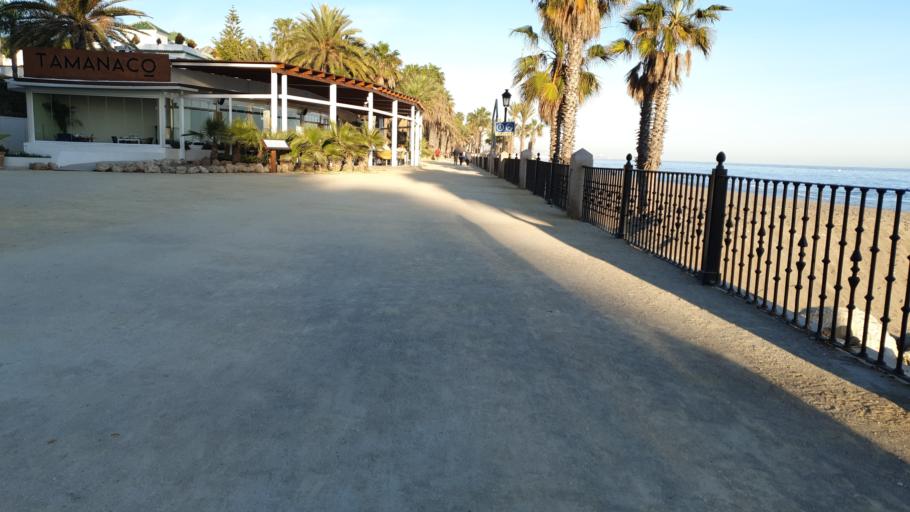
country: ES
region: Andalusia
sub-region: Provincia de Malaga
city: Marbella
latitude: 36.5060
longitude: -4.9123
